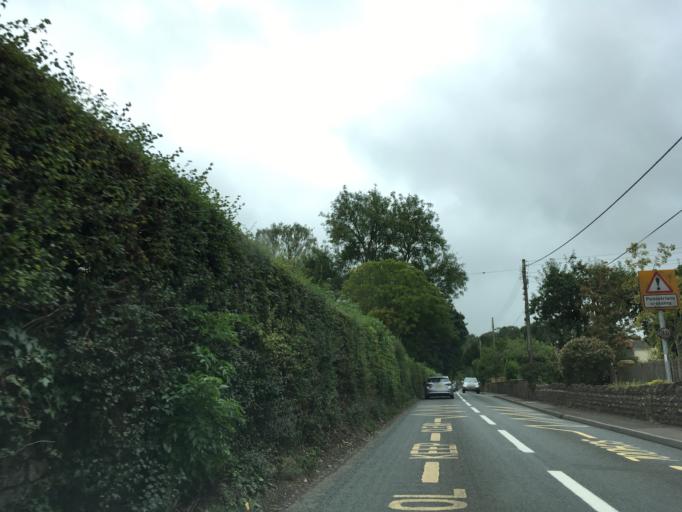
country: GB
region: England
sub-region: Bath and North East Somerset
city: Cameley
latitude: 51.2758
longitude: -2.5781
